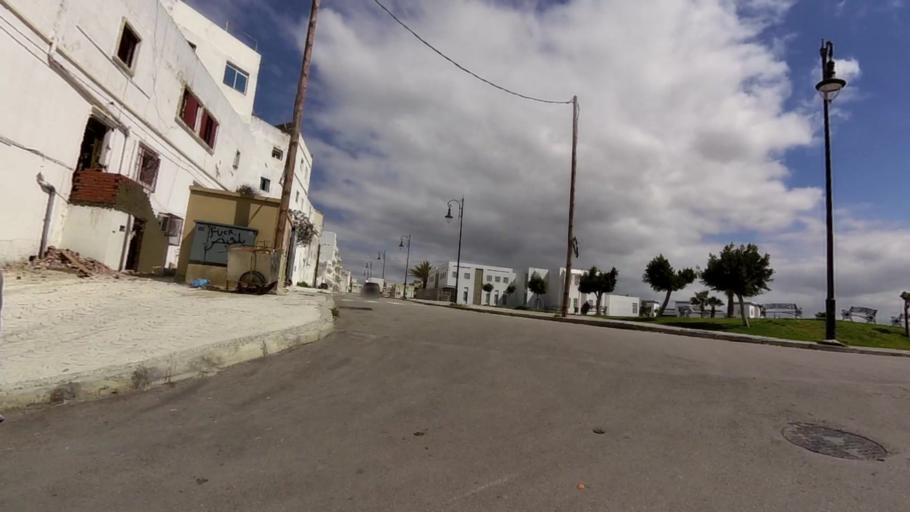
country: MA
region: Tanger-Tetouan
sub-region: Tanger-Assilah
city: Tangier
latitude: 35.7565
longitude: -5.8077
